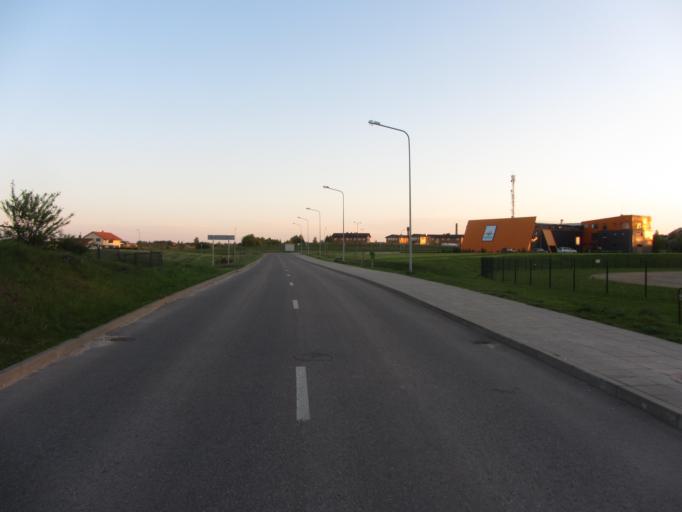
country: LT
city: Moletai
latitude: 55.2253
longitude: 25.4201
